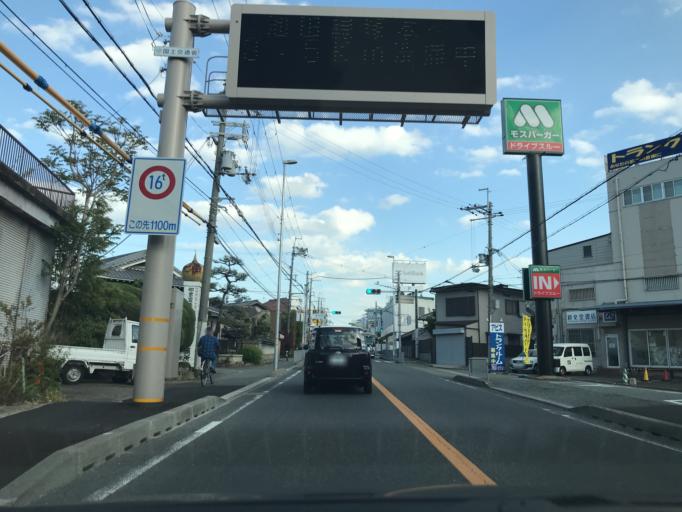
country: JP
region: Osaka
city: Ikeda
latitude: 34.8158
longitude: 135.4369
